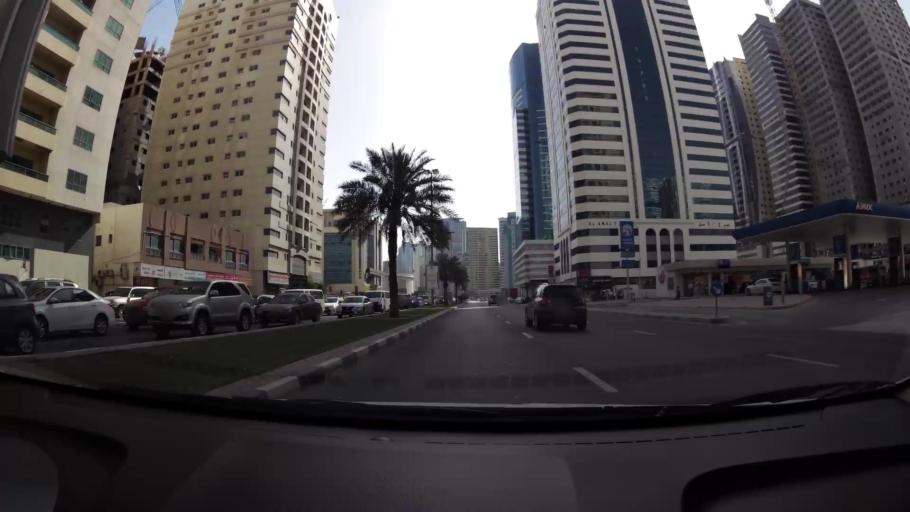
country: AE
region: Ash Shariqah
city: Sharjah
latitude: 25.3065
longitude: 55.3665
